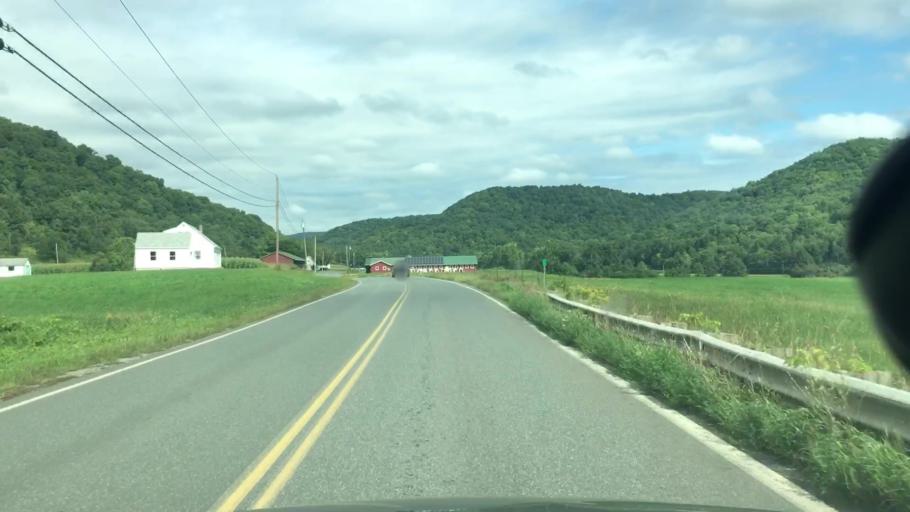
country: US
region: Massachusetts
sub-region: Franklin County
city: Colrain
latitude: 42.6938
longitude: -72.6939
